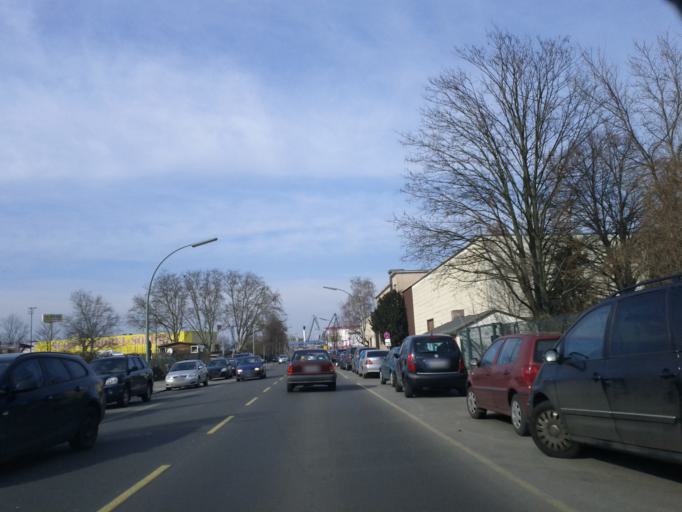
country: DE
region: Berlin
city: Plaenterwald
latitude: 52.4629
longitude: 13.4597
